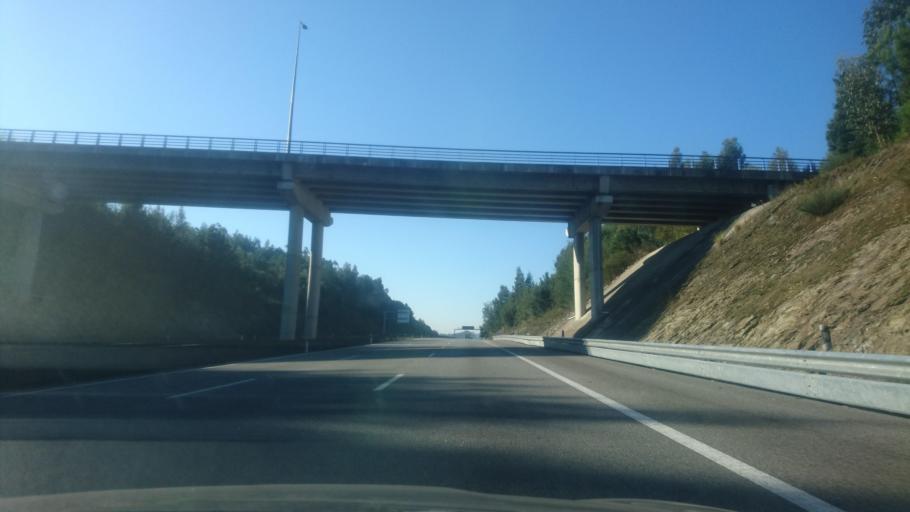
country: PT
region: Porto
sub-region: Vila Nova de Gaia
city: Sandim
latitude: 41.0552
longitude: -8.4709
